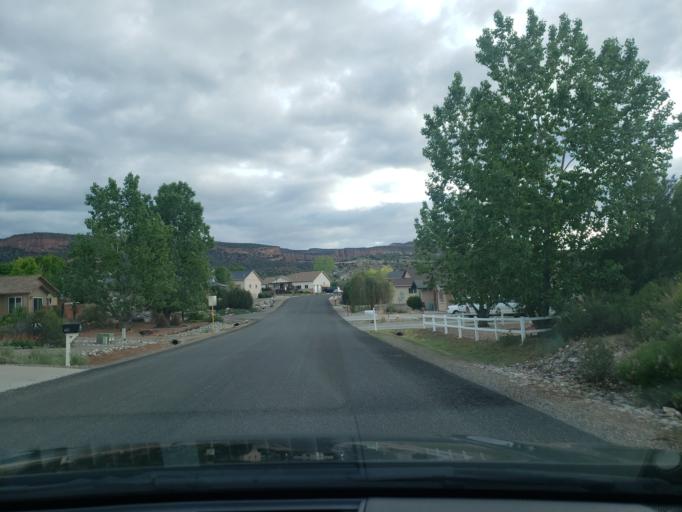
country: US
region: Colorado
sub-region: Mesa County
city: Fruita
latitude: 39.1376
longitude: -108.7434
